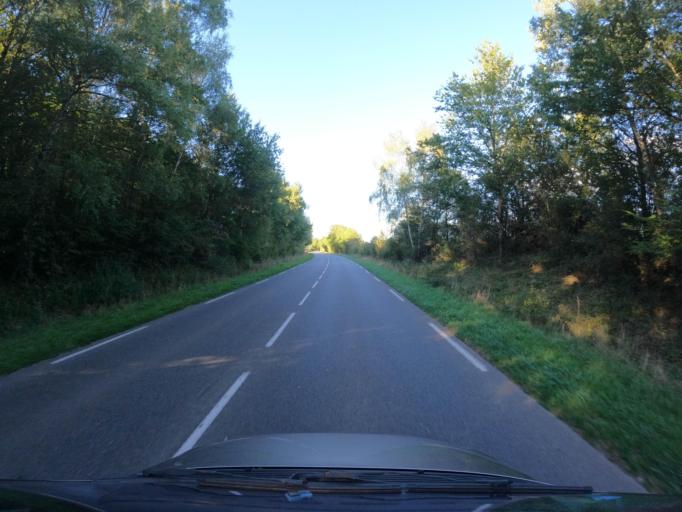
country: FR
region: Bourgogne
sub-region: Departement de Saone-et-Loire
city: Montchanin
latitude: 46.7388
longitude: 4.4449
